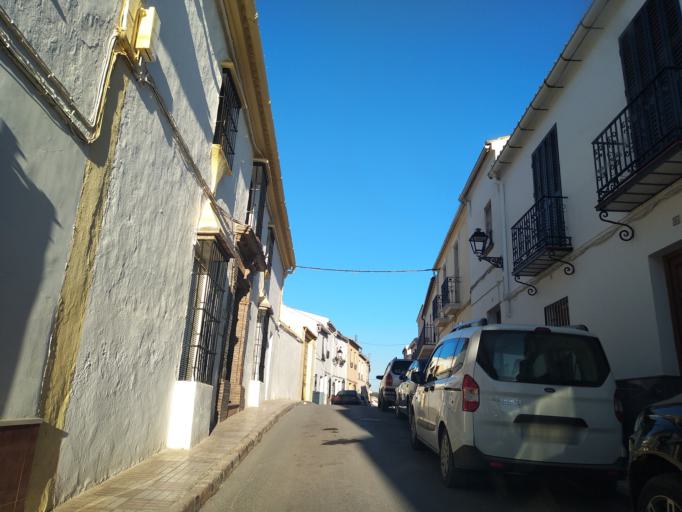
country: ES
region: Andalusia
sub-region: Provincia de Malaga
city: Campillos
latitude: 37.0491
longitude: -4.8640
